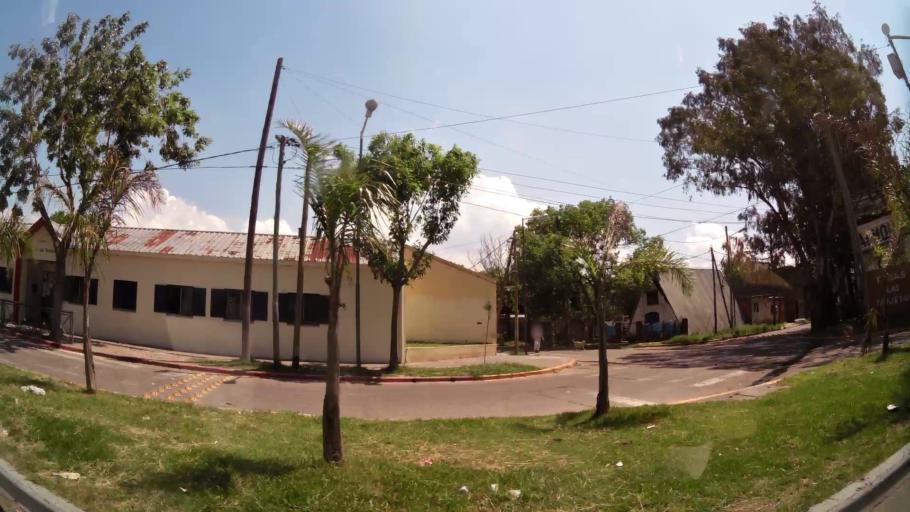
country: AR
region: Buenos Aires
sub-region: Partido de Tigre
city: Tigre
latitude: -34.4476
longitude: -58.5783
